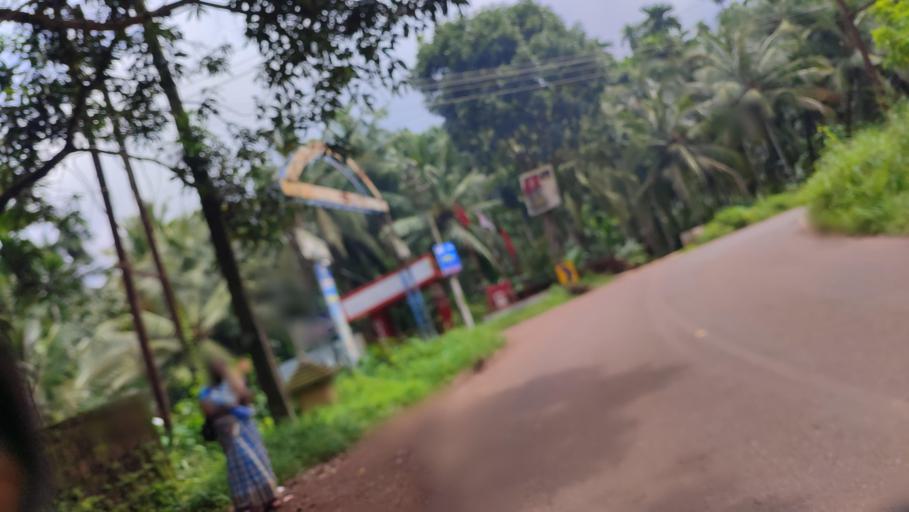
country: IN
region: Kerala
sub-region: Kasaragod District
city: Kannangad
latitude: 12.3957
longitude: 75.0538
